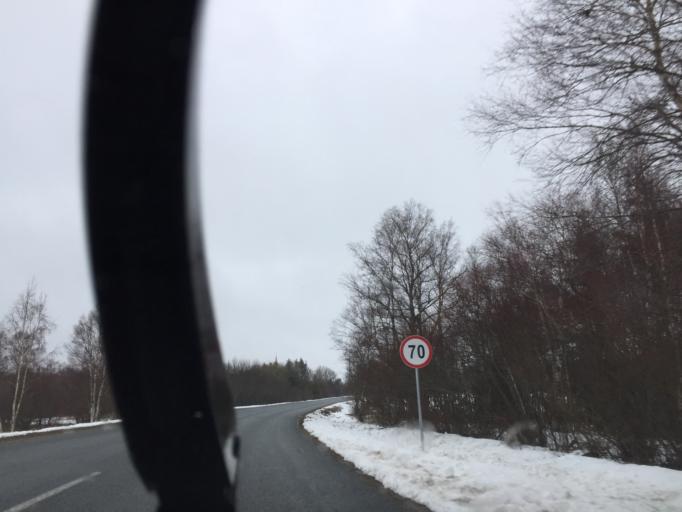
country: EE
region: Saare
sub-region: Kuressaare linn
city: Kuressaare
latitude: 58.3541
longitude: 22.0330
